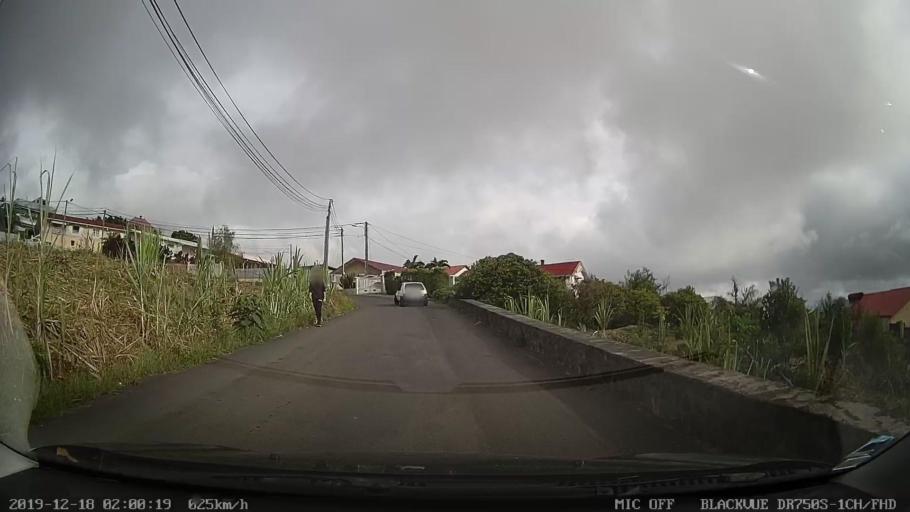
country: RE
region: Reunion
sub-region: Reunion
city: Le Tampon
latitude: -21.2539
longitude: 55.5174
